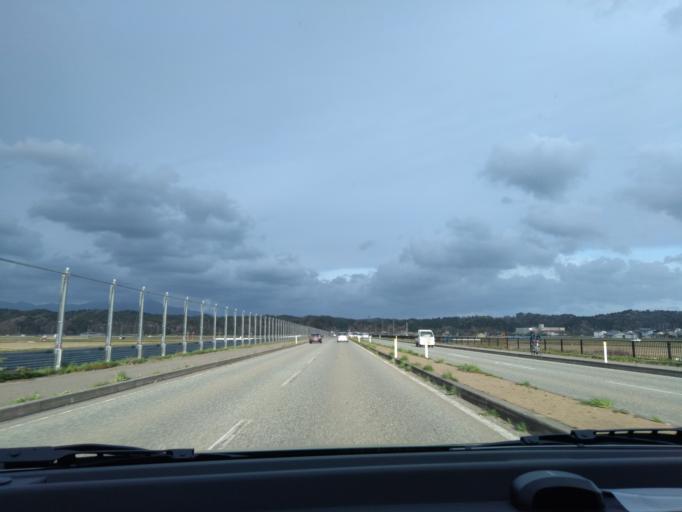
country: JP
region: Akita
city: Akita Shi
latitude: 39.7540
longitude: 140.1036
